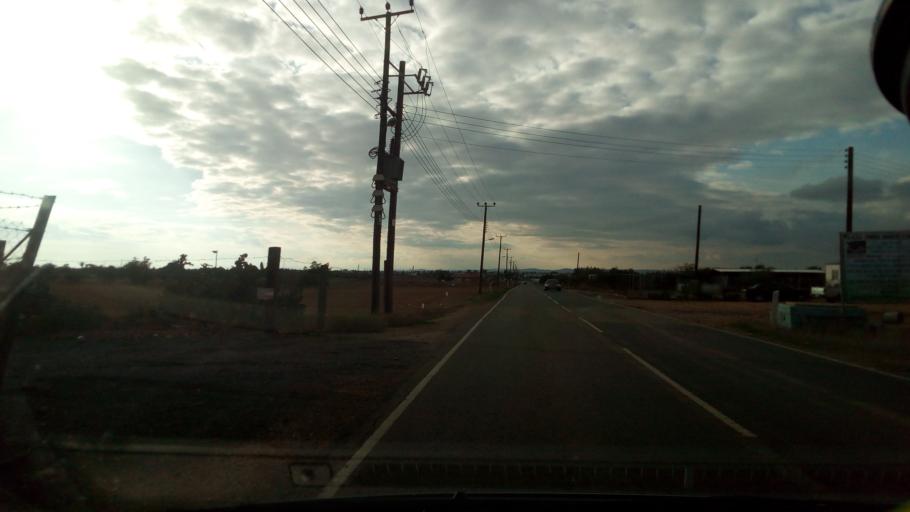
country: CY
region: Ammochostos
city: Avgorou
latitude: 35.0409
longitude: 33.8602
